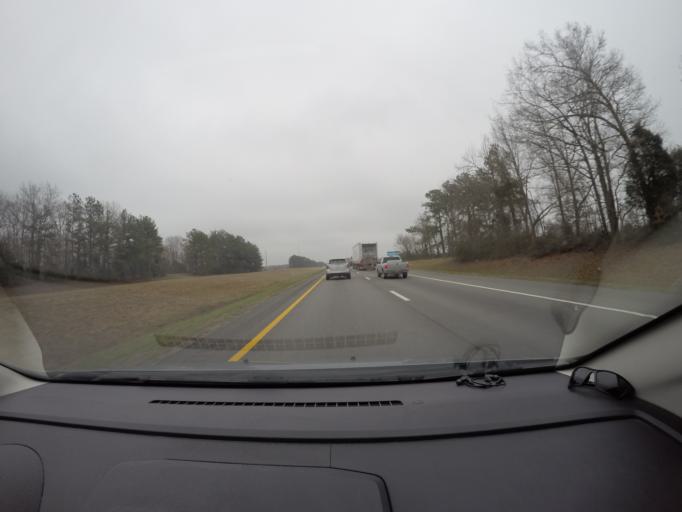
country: US
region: Tennessee
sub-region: Coffee County
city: New Union
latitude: 35.5192
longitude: -86.1264
